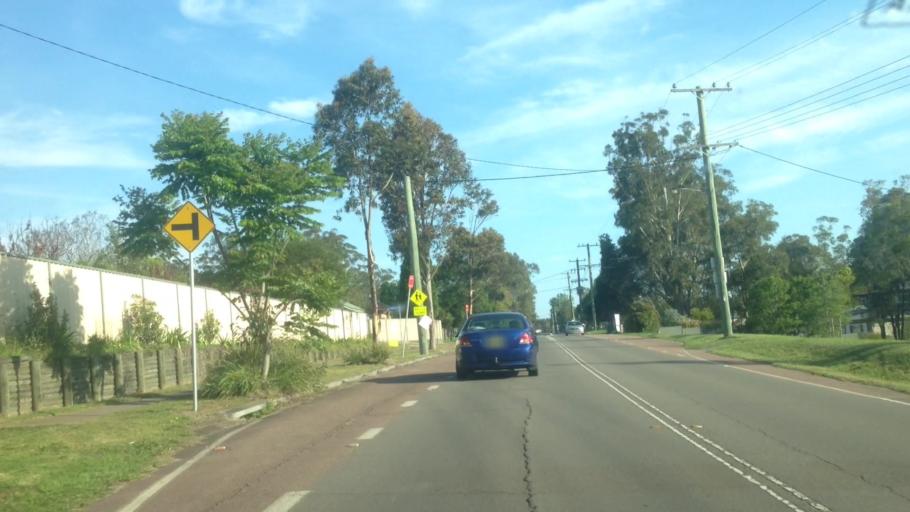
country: AU
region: New South Wales
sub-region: Lake Macquarie Shire
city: Cooranbong
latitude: -33.0957
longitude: 151.4720
